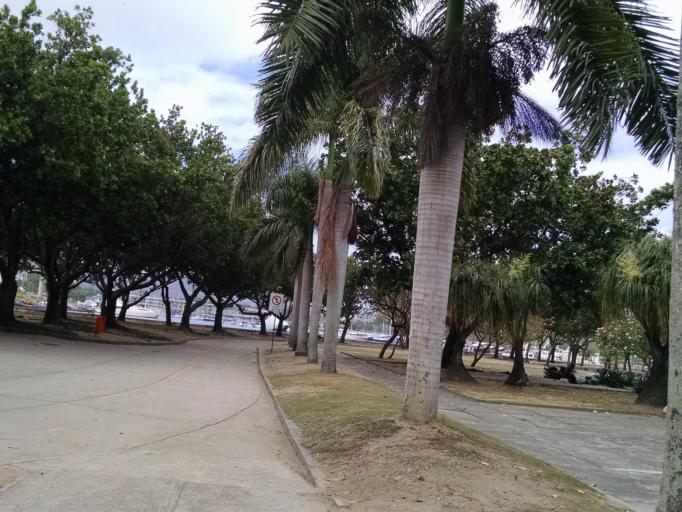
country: BR
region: Rio de Janeiro
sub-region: Rio De Janeiro
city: Rio de Janeiro
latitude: -22.9137
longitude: -43.1708
